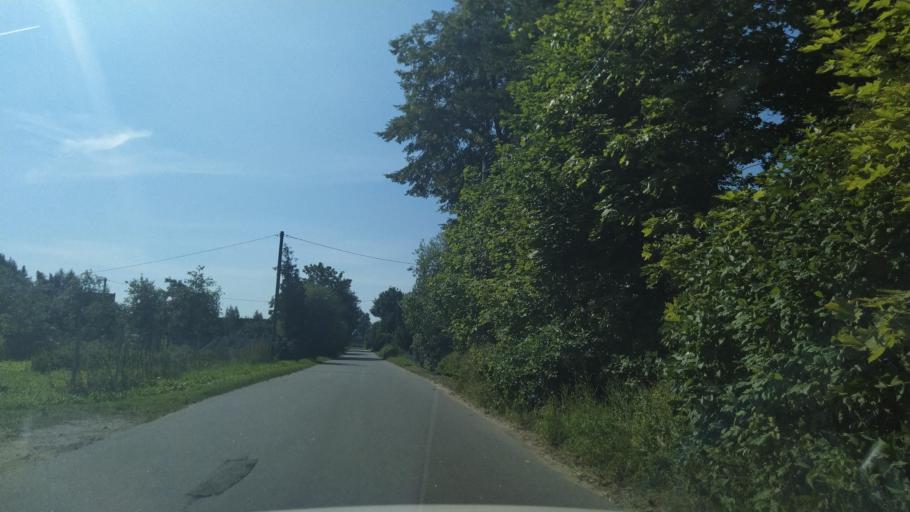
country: RU
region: Leningrad
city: Siverskiy
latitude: 59.2686
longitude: 30.0432
